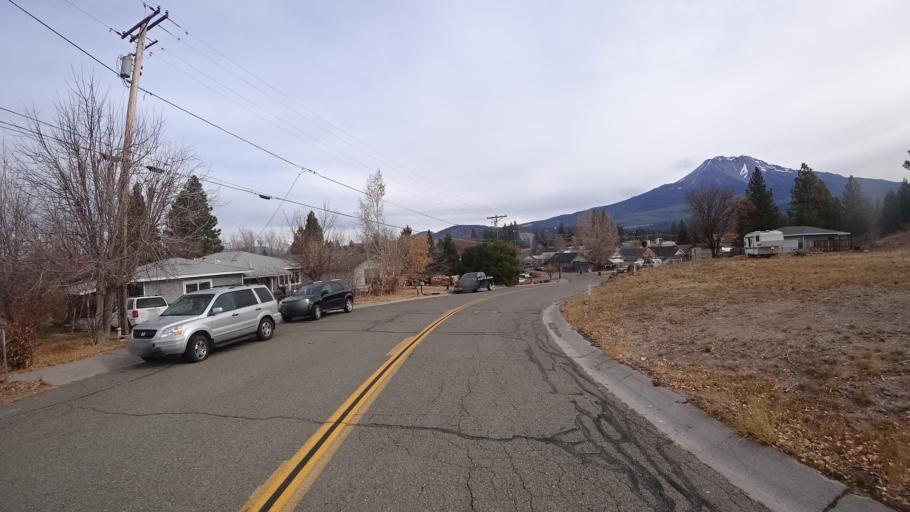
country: US
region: California
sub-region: Siskiyou County
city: Weed
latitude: 41.4283
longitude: -122.3777
